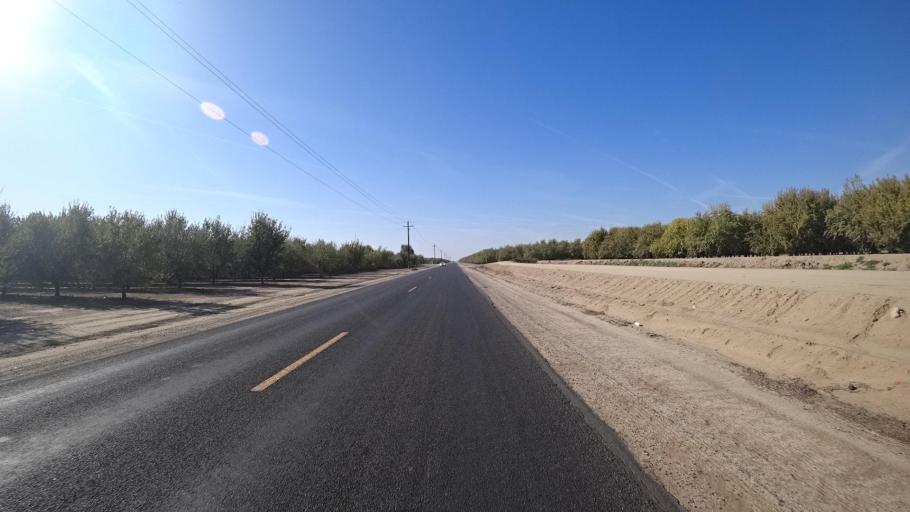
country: US
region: California
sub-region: Kern County
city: McFarland
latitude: 35.6454
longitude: -119.2669
